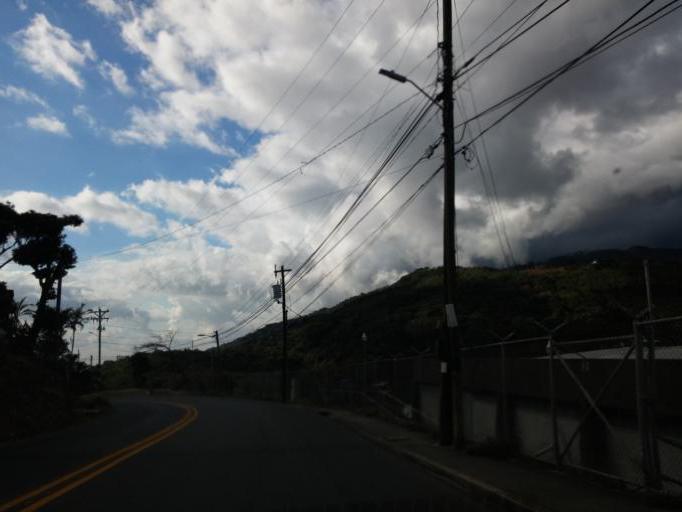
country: CR
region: San Jose
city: San Ignacio
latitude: 9.7972
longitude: -84.1328
